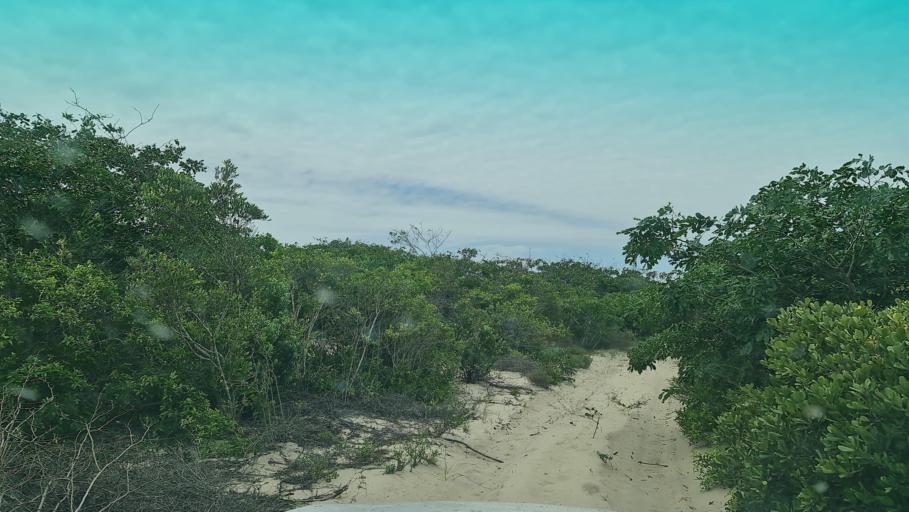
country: MZ
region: Maputo
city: Manhica
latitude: -25.6369
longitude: 32.7844
